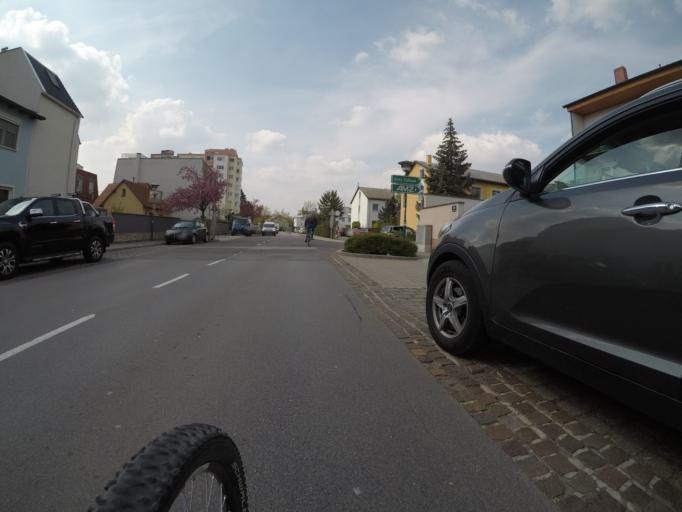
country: AT
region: Lower Austria
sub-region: Politischer Bezirk Modling
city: Wiener Neudorf
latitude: 48.0825
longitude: 16.3128
